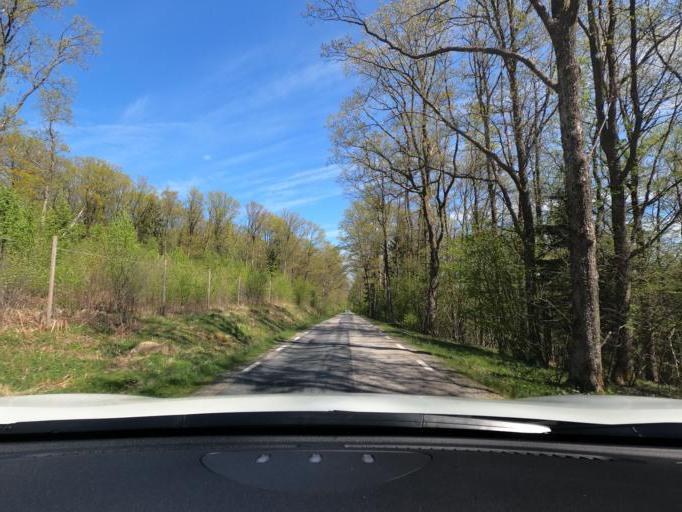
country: SE
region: Vaestra Goetaland
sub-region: Marks Kommun
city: Horred
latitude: 57.4344
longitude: 12.4150
